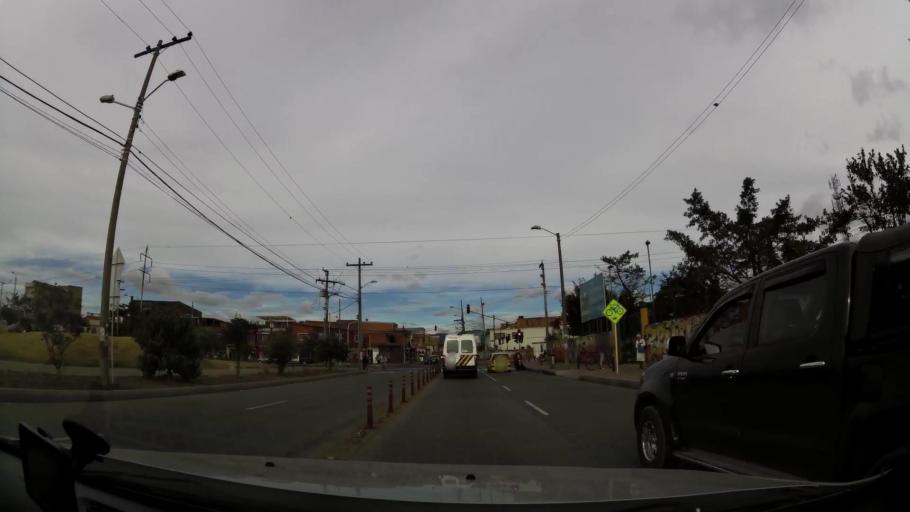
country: CO
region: Cundinamarca
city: Soacha
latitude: 4.6188
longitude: -74.1568
